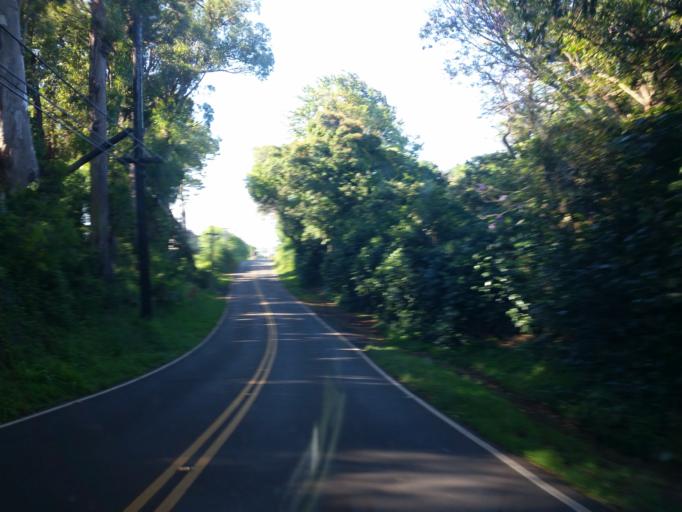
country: US
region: Hawaii
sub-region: Maui County
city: Makawao
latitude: 20.8454
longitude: -156.3086
